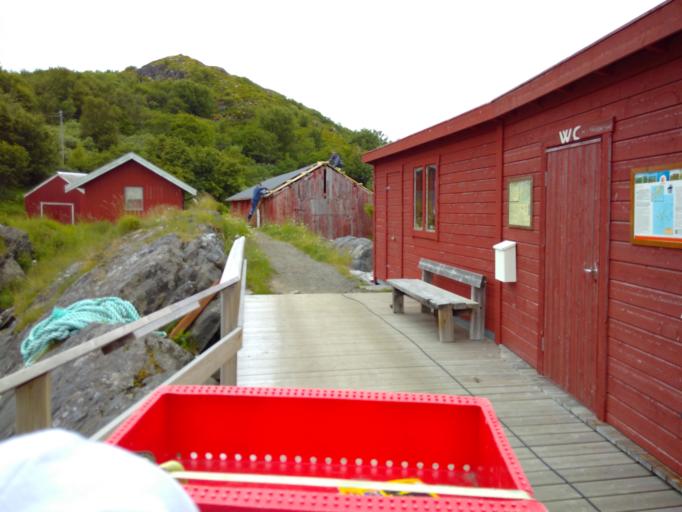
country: NO
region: Nordland
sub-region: Gildeskal
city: Inndyr
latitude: 67.2769
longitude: 14.0064
